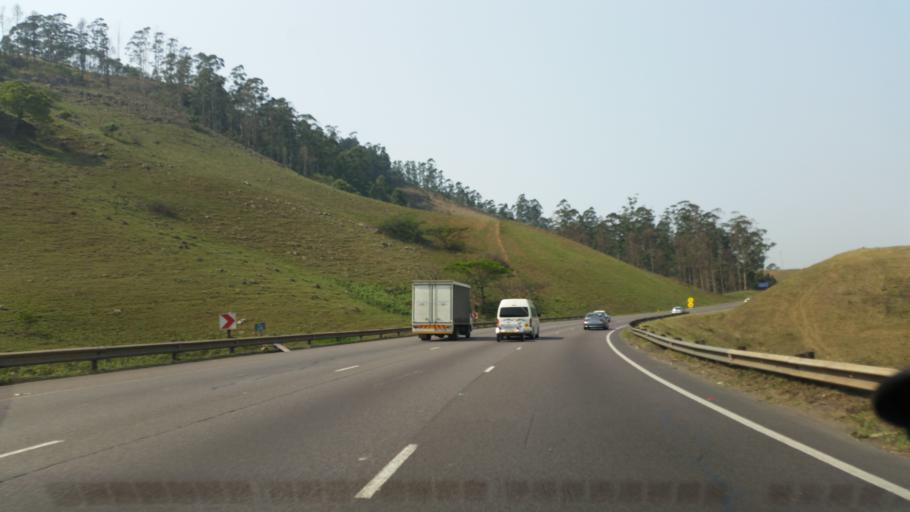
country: ZA
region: KwaZulu-Natal
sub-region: eThekwini Metropolitan Municipality
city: Mpumalanga
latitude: -29.7791
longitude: 30.7102
